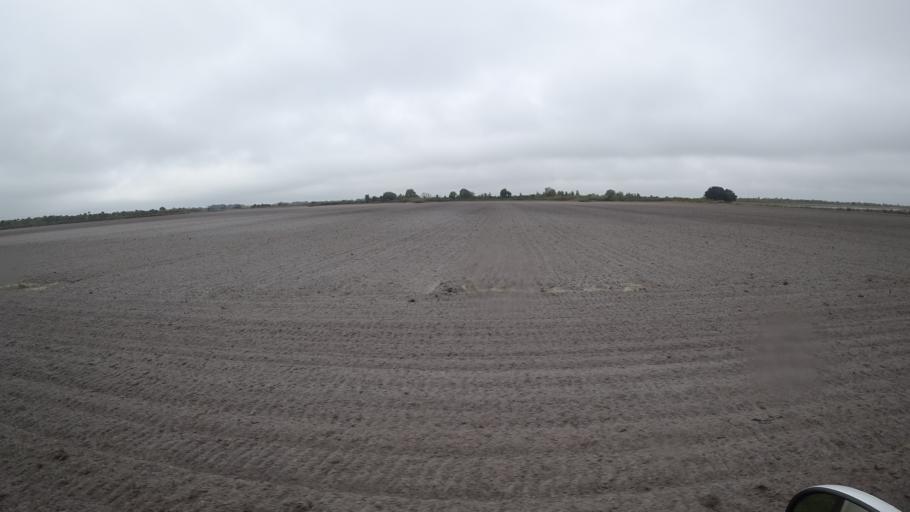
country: US
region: Florida
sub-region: Sarasota County
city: Warm Mineral Springs
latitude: 27.2839
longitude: -82.1755
